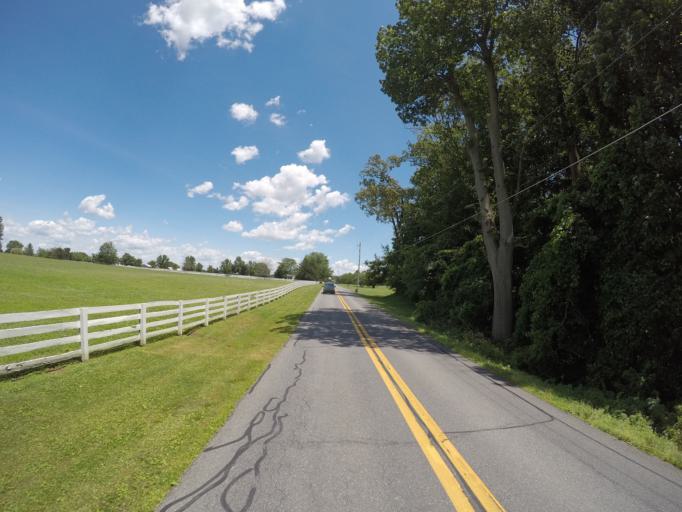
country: US
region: Delaware
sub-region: New Castle County
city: Middletown
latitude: 39.4811
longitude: -75.7589
